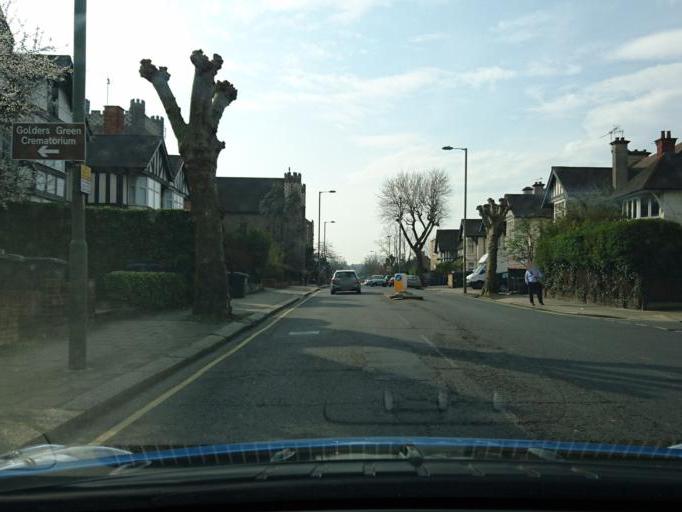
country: GB
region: England
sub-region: Greater London
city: Hendon
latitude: 51.5772
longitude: -0.1970
